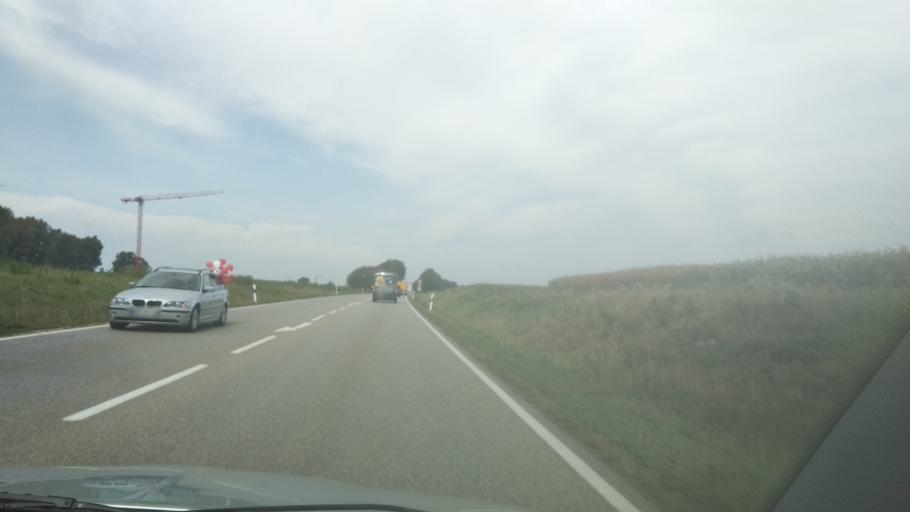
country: DE
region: Bavaria
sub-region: Upper Bavaria
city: Ismaning
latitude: 48.2195
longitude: 11.6902
